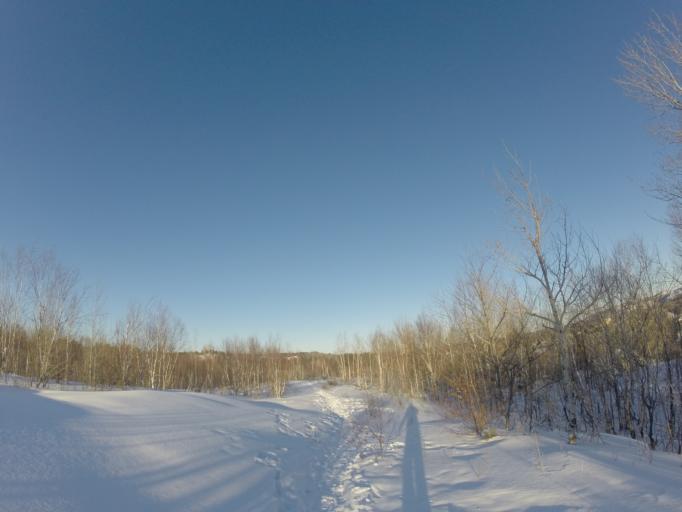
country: CA
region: Ontario
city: Greater Sudbury
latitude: 46.5051
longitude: -80.9995
